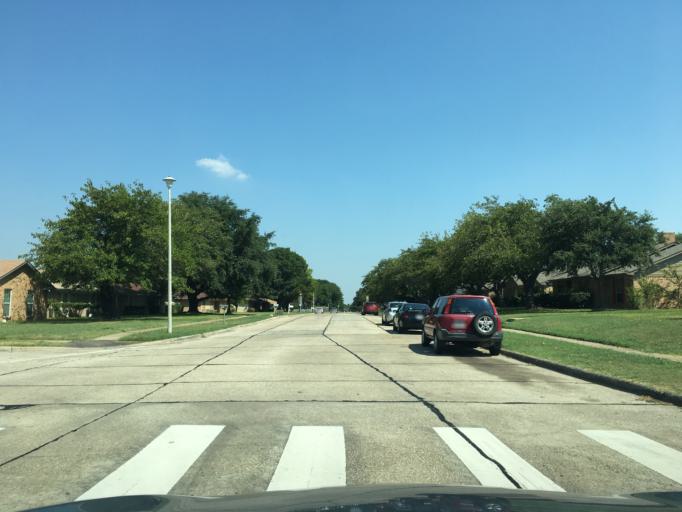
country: US
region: Texas
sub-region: Dallas County
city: Garland
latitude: 32.9359
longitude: -96.6572
